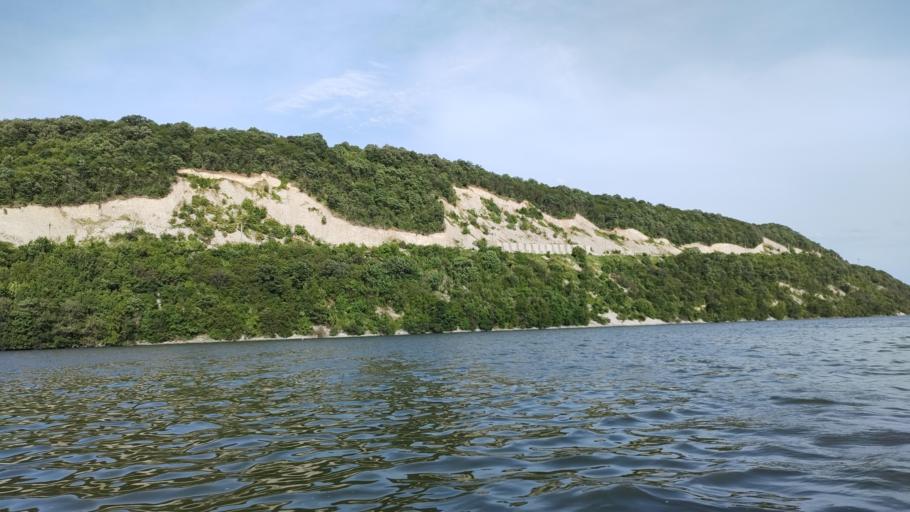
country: RO
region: Mehedinti
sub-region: Comuna Svinita
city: Svinita
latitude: 44.5126
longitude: 22.0784
